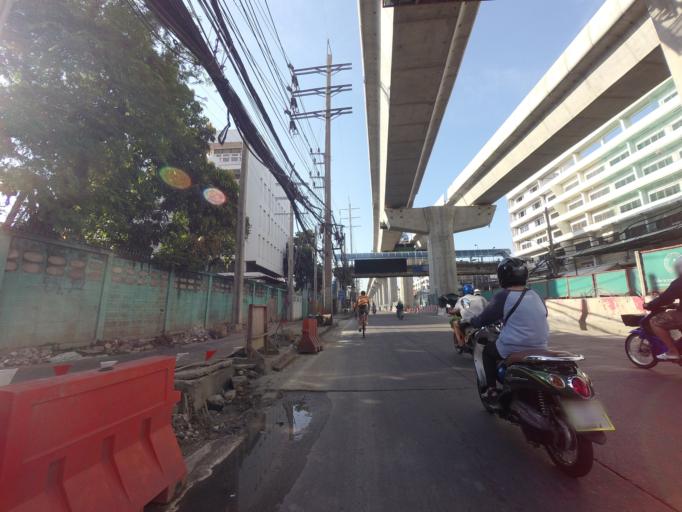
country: TH
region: Samut Prakan
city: Samut Prakan
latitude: 13.6450
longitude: 100.5953
